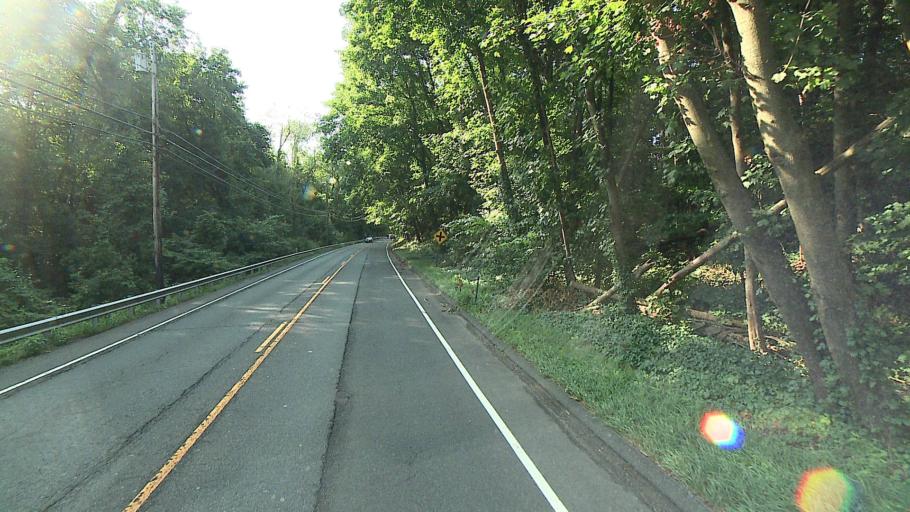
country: US
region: Connecticut
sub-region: Fairfield County
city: Georgetown
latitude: 41.2325
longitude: -73.4278
